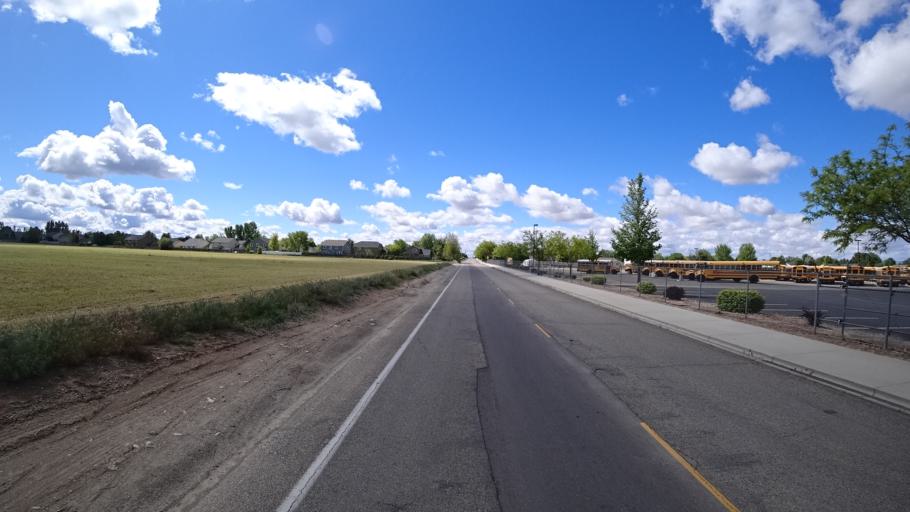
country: US
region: Idaho
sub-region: Ada County
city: Kuna
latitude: 43.4971
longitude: -116.4039
